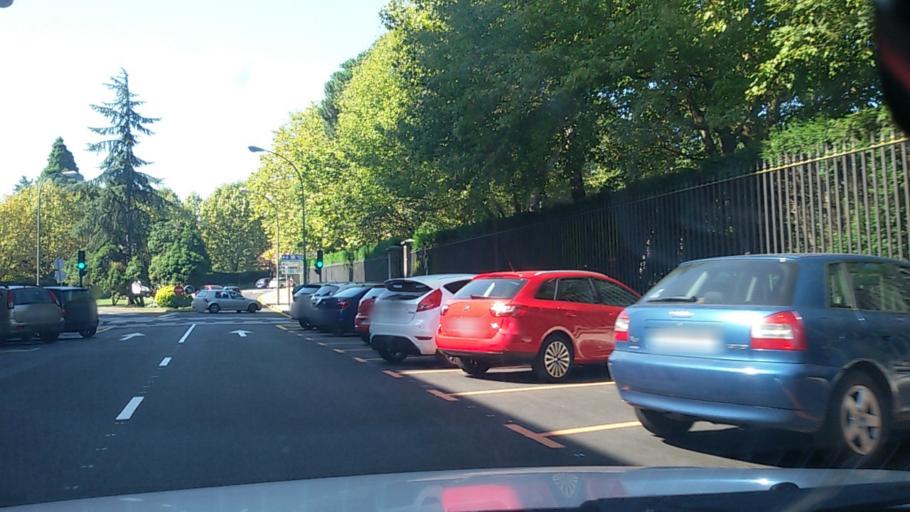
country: ES
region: Asturias
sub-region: Province of Asturias
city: Aviles
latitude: 43.5518
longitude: -5.9223
